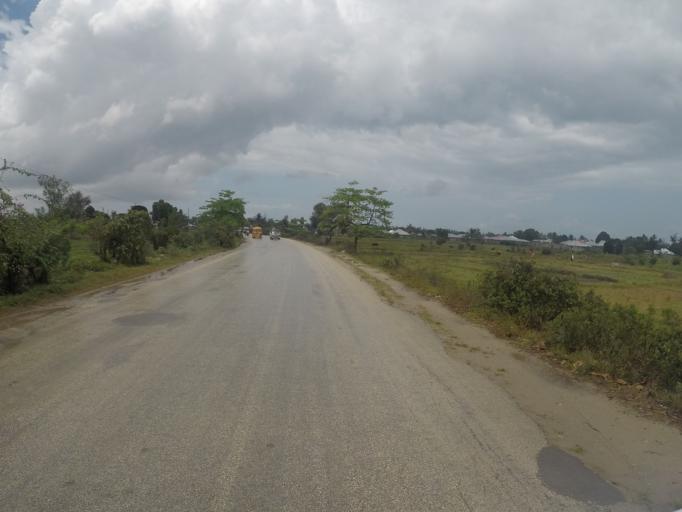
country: TZ
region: Zanzibar Central/South
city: Koani
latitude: -6.0768
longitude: 39.2226
